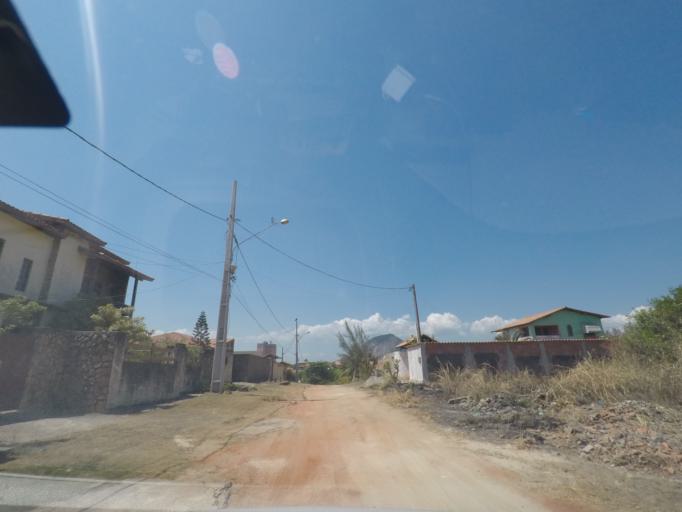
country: BR
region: Rio de Janeiro
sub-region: Marica
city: Marica
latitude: -22.9739
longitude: -42.9198
